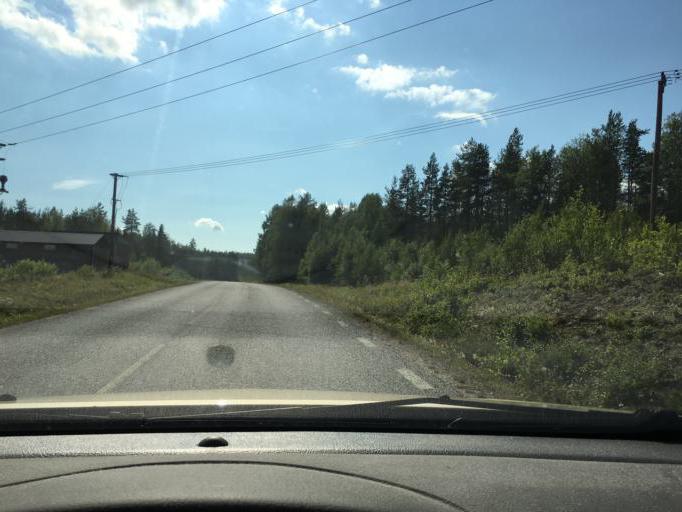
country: SE
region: Norrbotten
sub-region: Kalix Kommun
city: Toere
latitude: 66.0673
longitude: 22.6834
